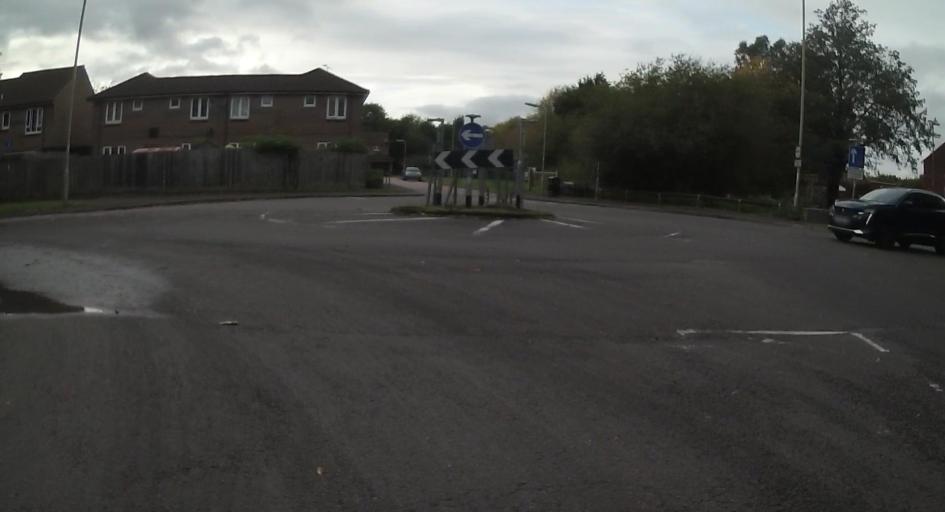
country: GB
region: England
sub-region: Hampshire
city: Farnborough
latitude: 51.2852
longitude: -0.7717
